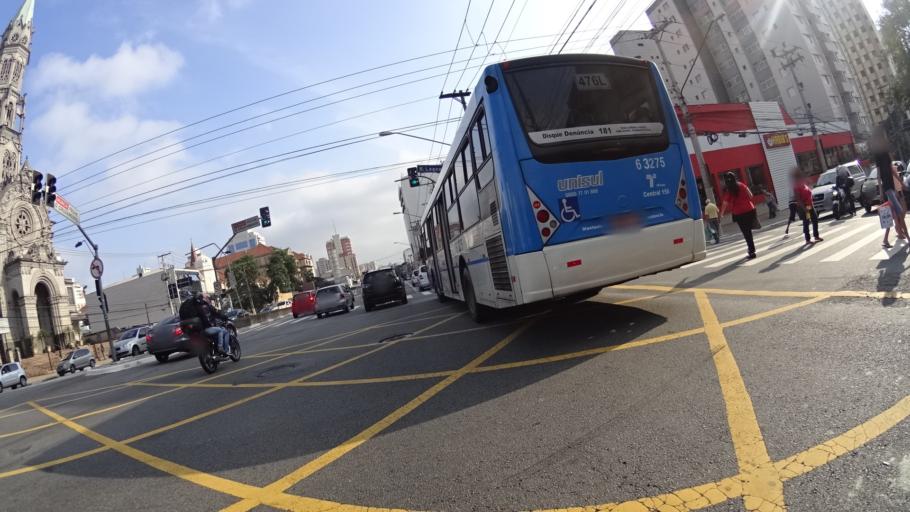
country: BR
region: Sao Paulo
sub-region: Sao Paulo
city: Sao Paulo
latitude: -23.5970
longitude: -46.6367
